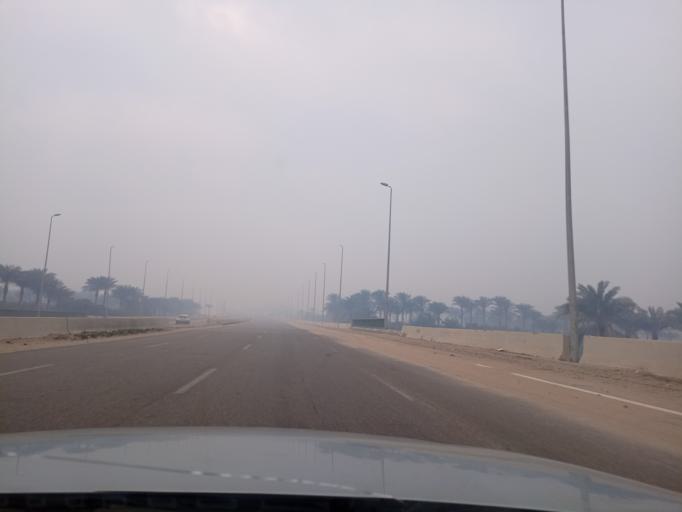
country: EG
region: Al Jizah
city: Al `Ayyat
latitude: 29.6842
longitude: 31.2376
